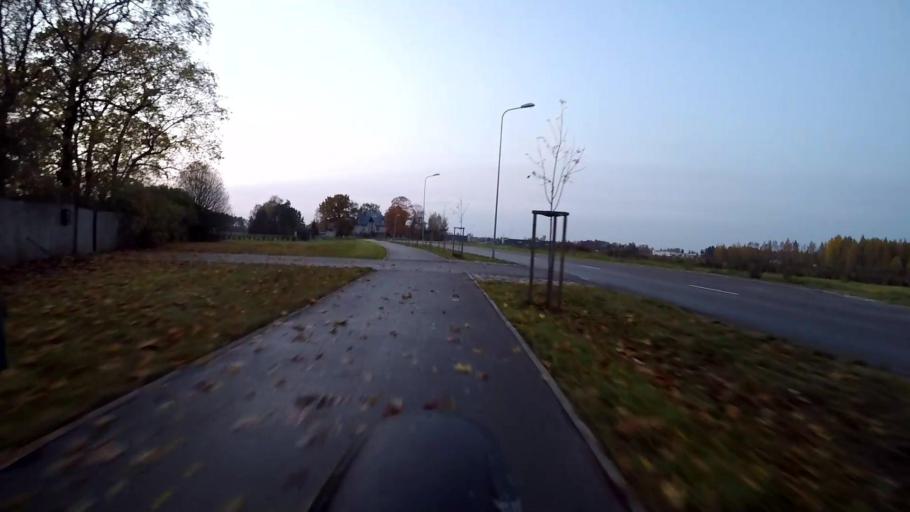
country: LV
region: Marupe
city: Marupe
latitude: 56.9115
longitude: 23.9971
